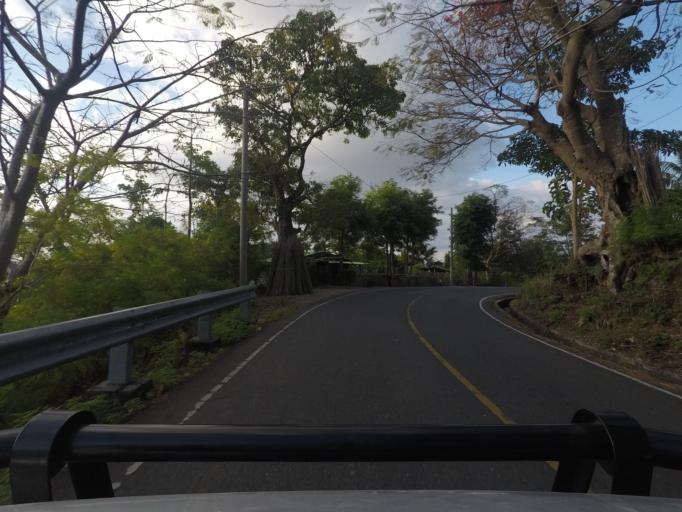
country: TL
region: Bobonaro
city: Maliana
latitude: -8.9560
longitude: 125.0637
